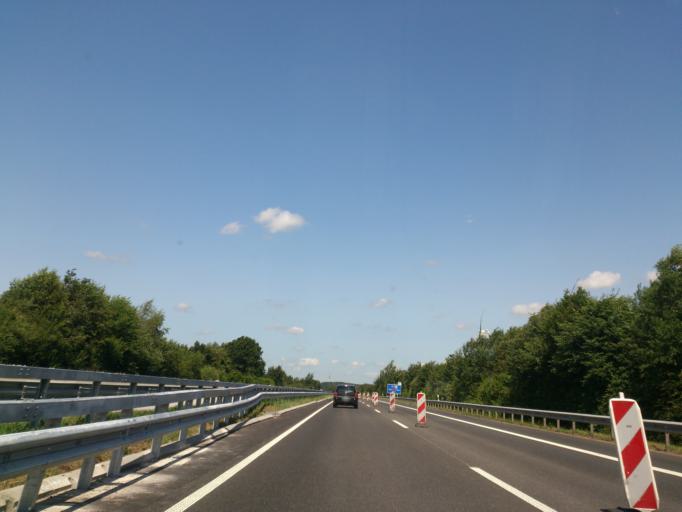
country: DE
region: Schleswig-Holstein
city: Tensbuttel-Rost
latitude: 54.1285
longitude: 9.2549
